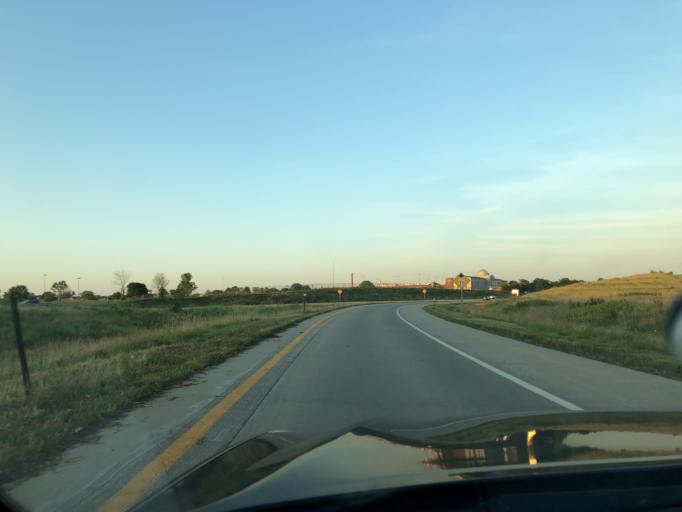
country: US
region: Kansas
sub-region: Leavenworth County
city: Leavenworth
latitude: 39.3275
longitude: -94.9481
